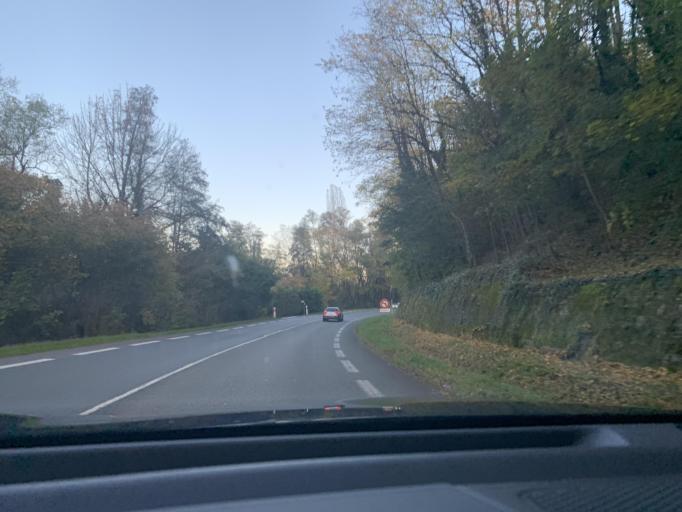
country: FR
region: Rhone-Alpes
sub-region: Departement du Rhone
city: Liergues
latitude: 45.9792
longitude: 4.6803
